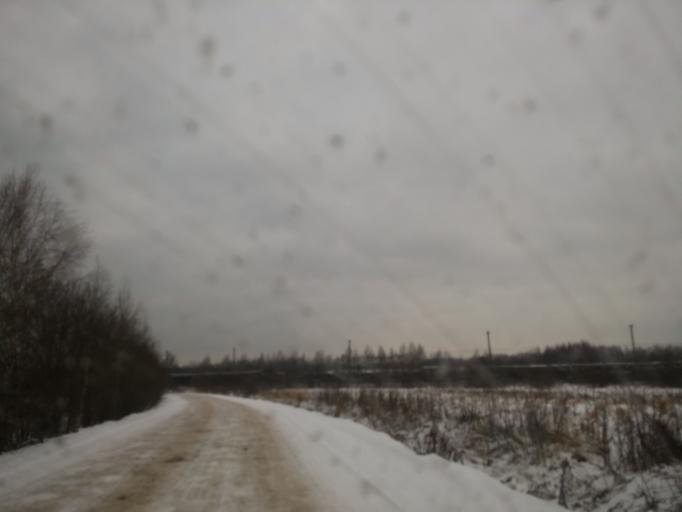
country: RU
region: Moskovskaya
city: Reshetnikovo
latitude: 56.4570
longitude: 36.5492
